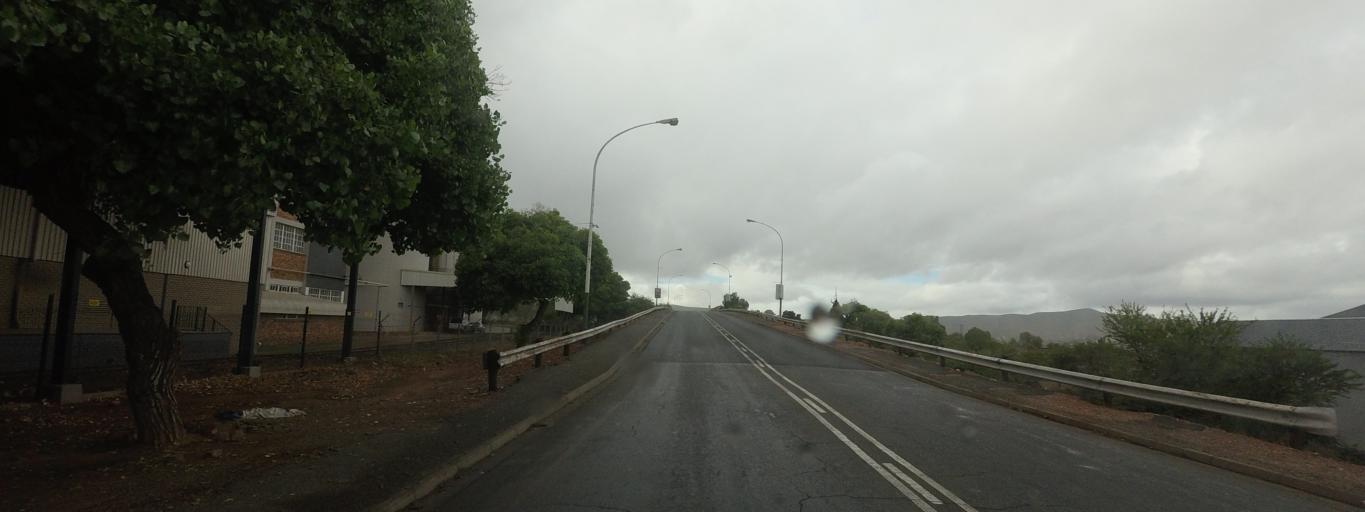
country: ZA
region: Western Cape
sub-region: Eden District Municipality
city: Oudtshoorn
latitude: -33.6094
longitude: 22.2129
